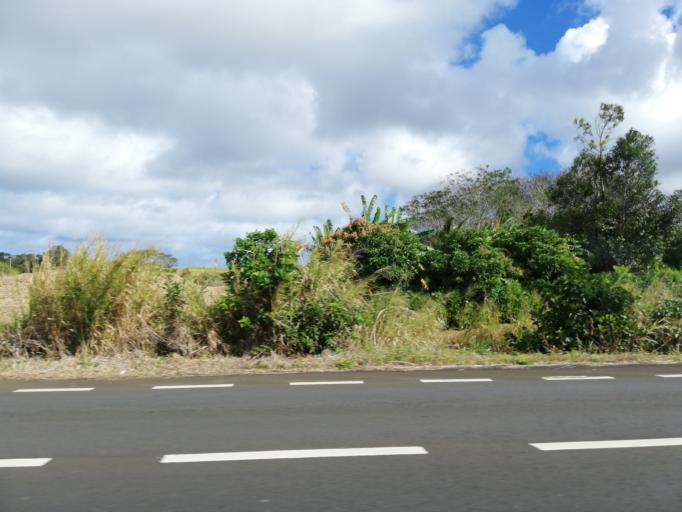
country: MU
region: Grand Port
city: Mahebourg
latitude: -20.4023
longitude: 57.6828
